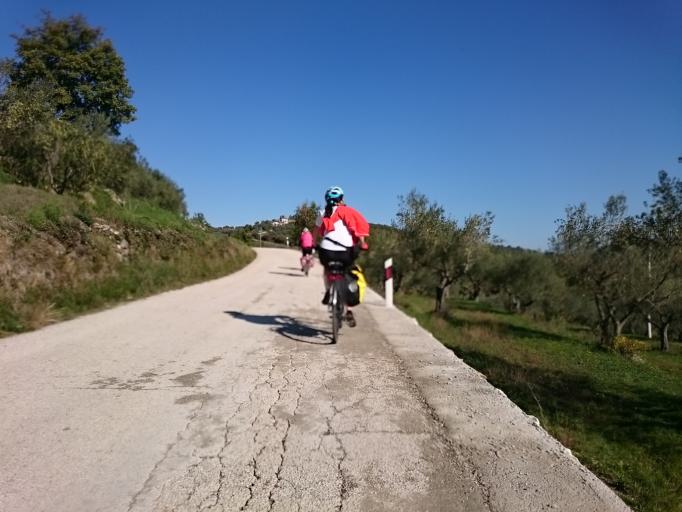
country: HR
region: Istarska
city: Buje
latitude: 45.4385
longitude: 13.6957
